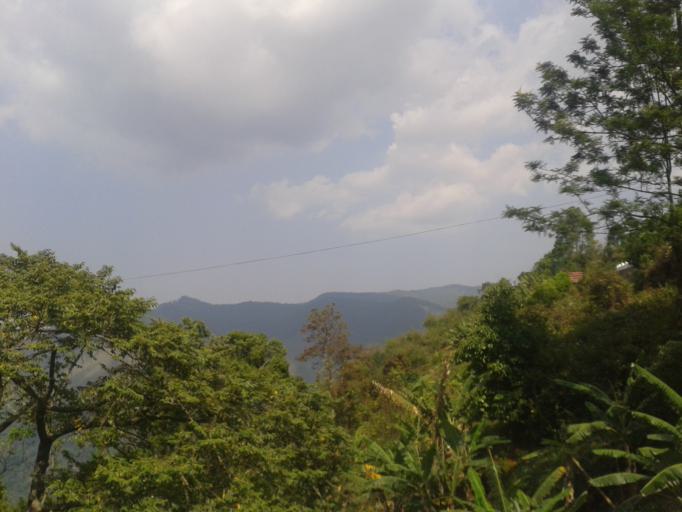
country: IN
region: Tamil Nadu
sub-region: Dindigul
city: Kodaikanal
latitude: 10.3256
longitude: 77.5635
